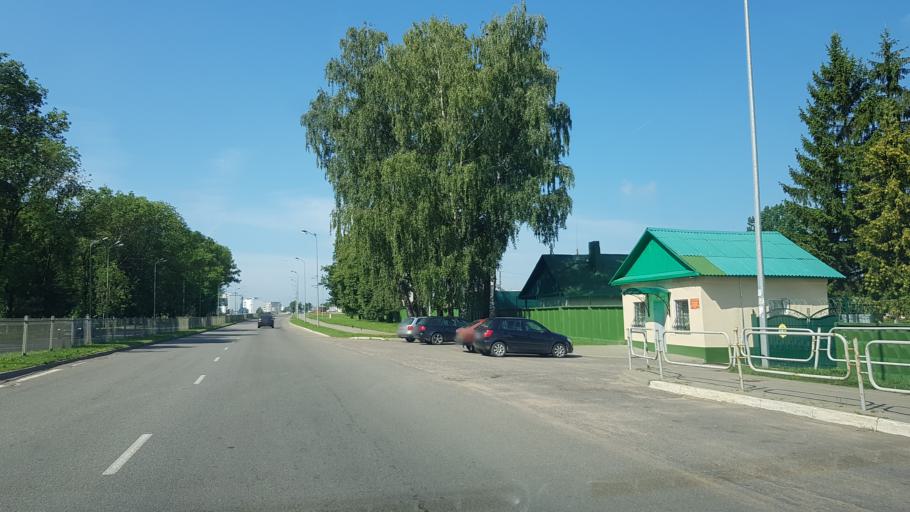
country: BY
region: Minsk
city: Dzyarzhynsk
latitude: 53.6886
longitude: 27.1578
